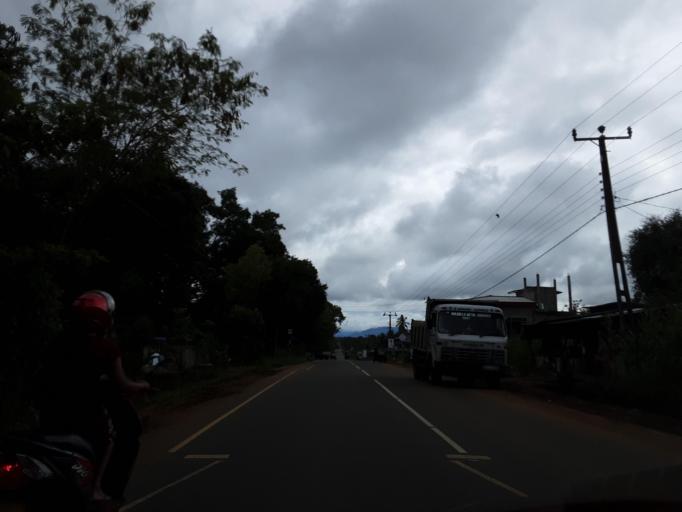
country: LK
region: Uva
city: Badulla
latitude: 7.3784
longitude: 81.0696
